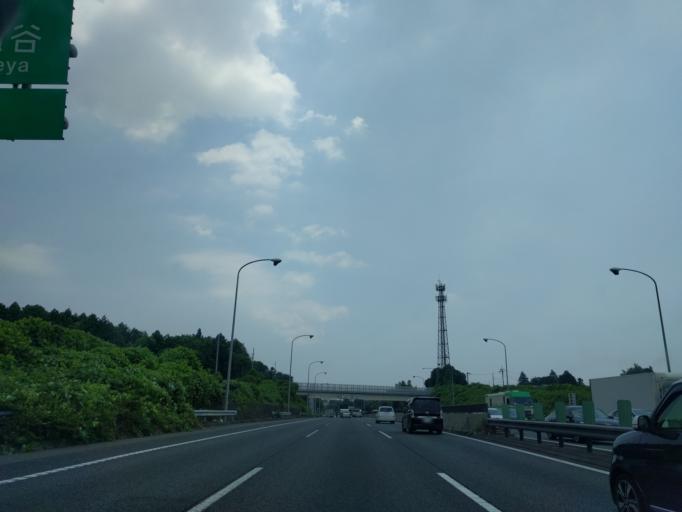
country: JP
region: Kanagawa
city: Minami-rinkan
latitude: 35.4875
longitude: 139.5079
